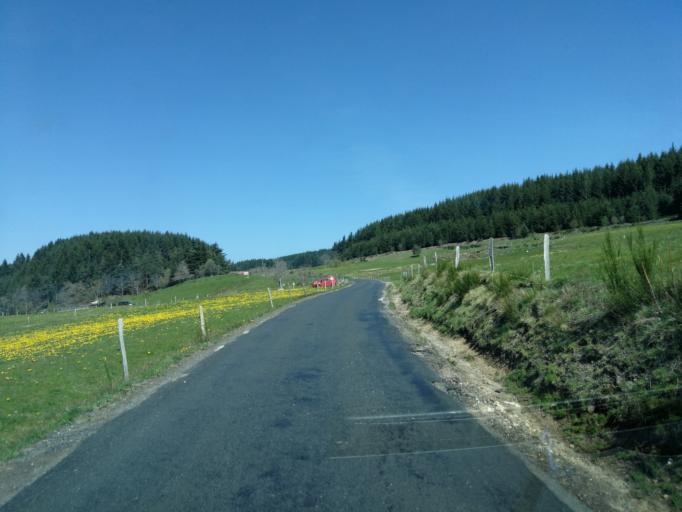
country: FR
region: Rhone-Alpes
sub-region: Departement de l'Ardeche
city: Le Cheylard
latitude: 44.9418
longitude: 4.4219
